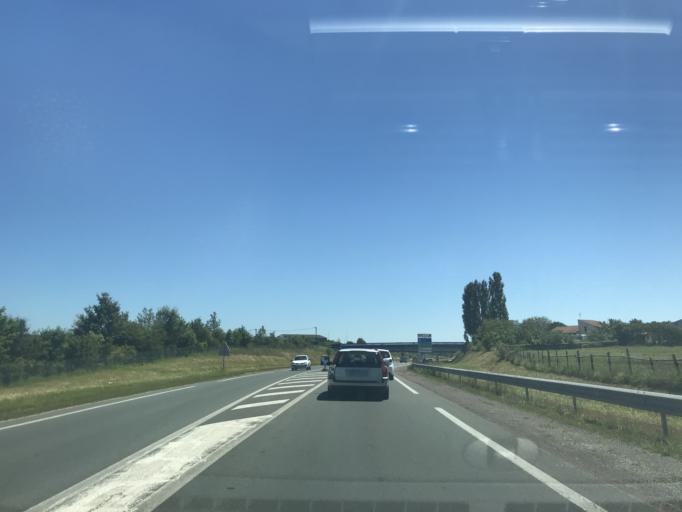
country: FR
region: Poitou-Charentes
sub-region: Departement de la Charente-Maritime
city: Saint-Georges-de-Didonne
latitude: 45.6085
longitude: -0.9761
